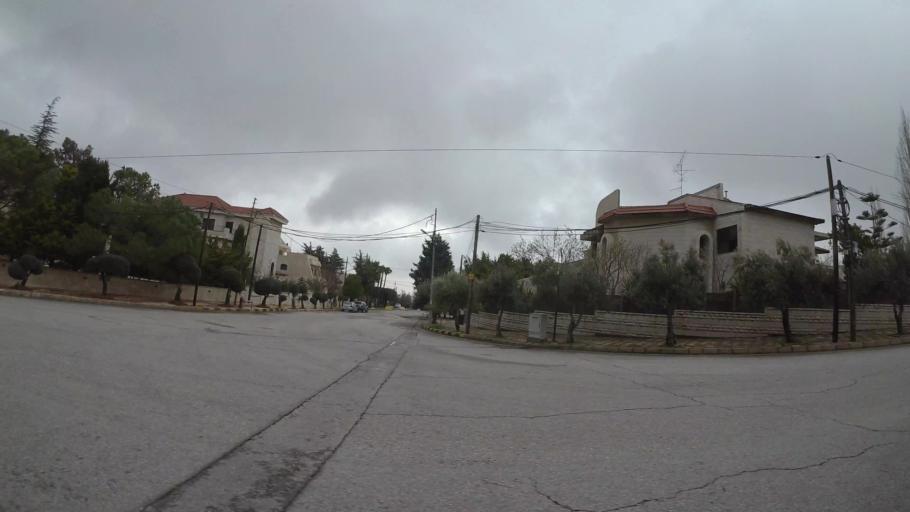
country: JO
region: Amman
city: Al Bunayyat ash Shamaliyah
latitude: 31.9379
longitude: 35.8820
